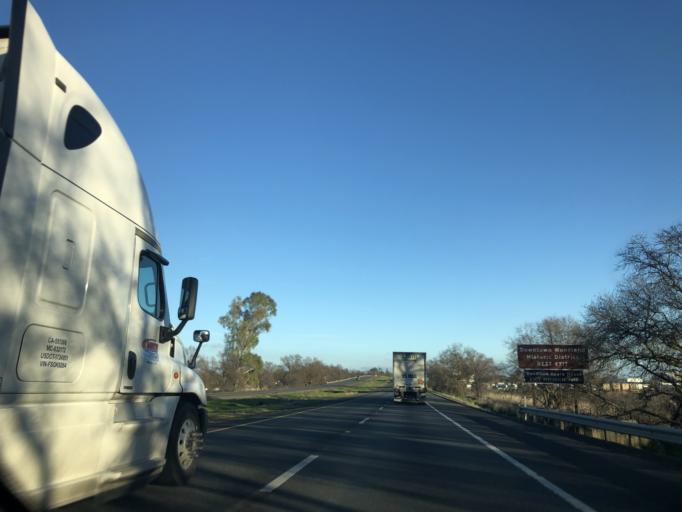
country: US
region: California
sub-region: Yolo County
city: Woodland
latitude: 38.6980
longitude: -121.7727
